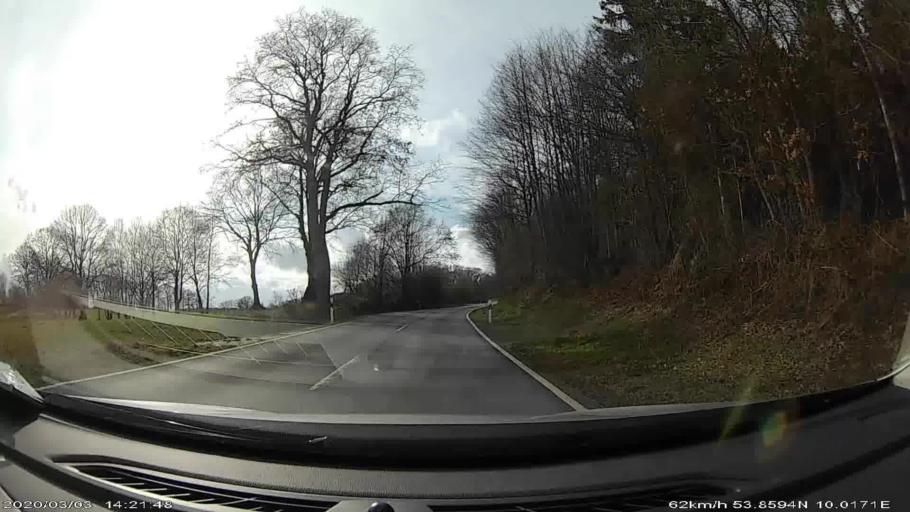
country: DE
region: Schleswig-Holstein
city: Kattendorf
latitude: 53.8593
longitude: 10.0168
